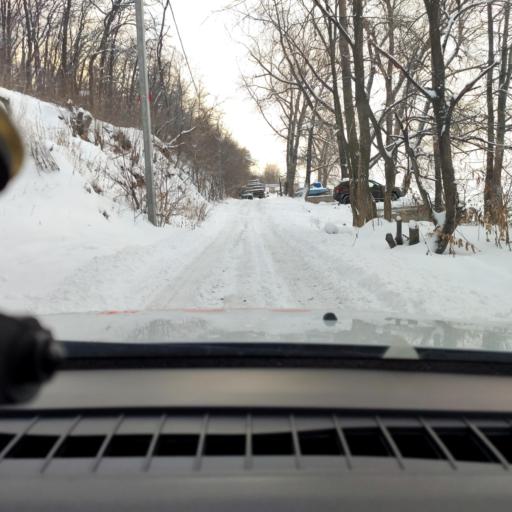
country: RU
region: Samara
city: Samara
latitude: 53.2889
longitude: 50.1916
